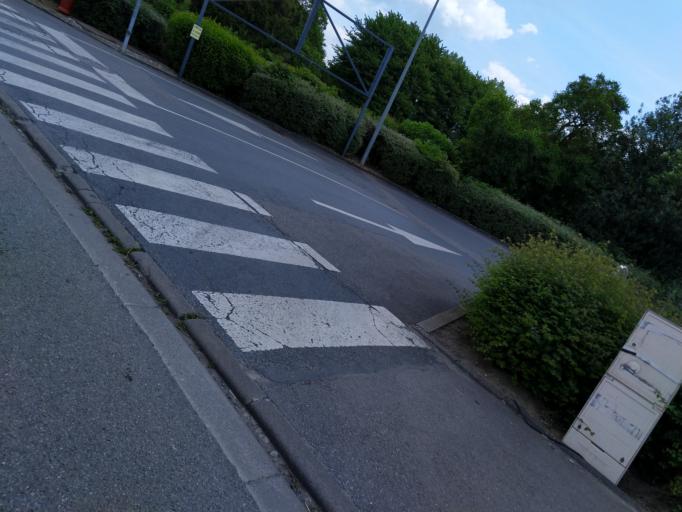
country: FR
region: Nord-Pas-de-Calais
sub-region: Departement du Nord
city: Le Quesnoy
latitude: 50.2525
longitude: 3.6421
